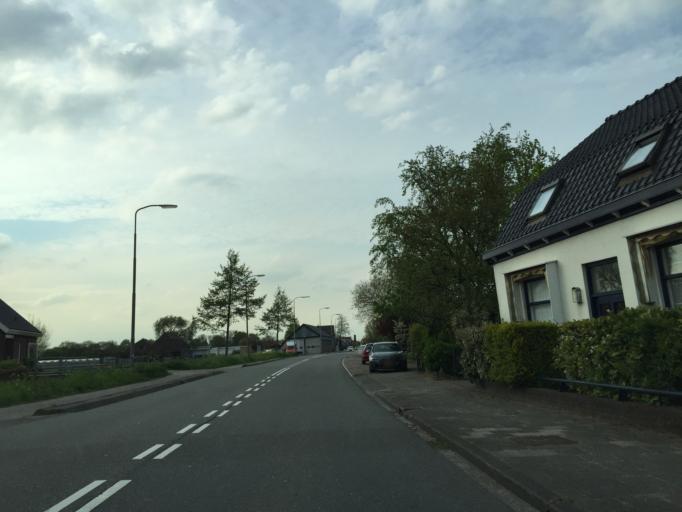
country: NL
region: South Holland
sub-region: Gemeente Pijnacker-Nootdorp
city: Pijnacker
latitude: 52.0255
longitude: 4.4351
